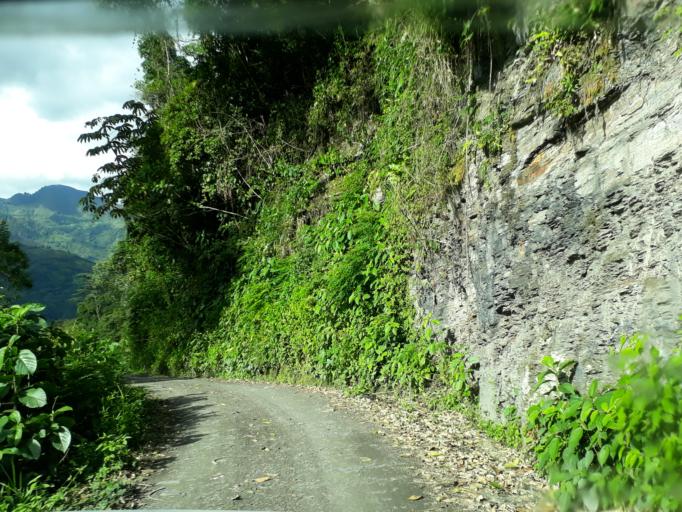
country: CO
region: Cundinamarca
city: Pacho
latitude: 5.1885
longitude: -74.2510
